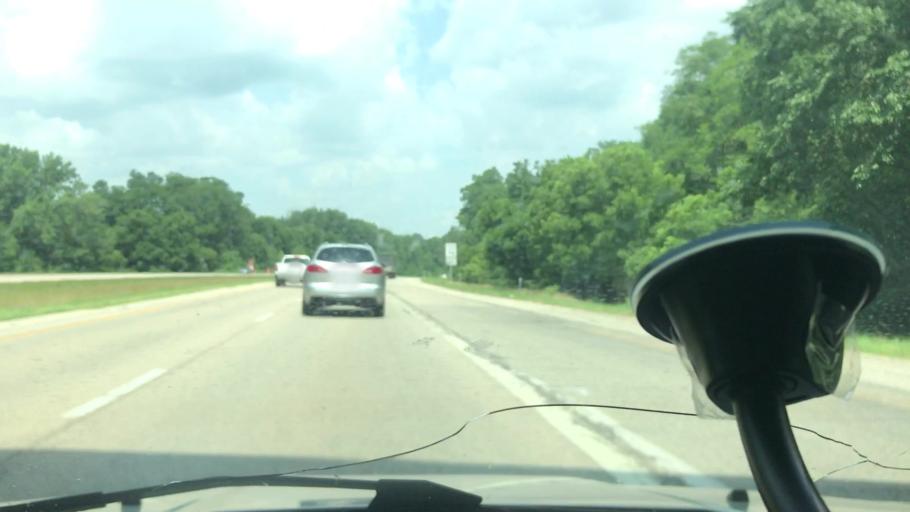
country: US
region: Illinois
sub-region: Peoria County
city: Bellevue
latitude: 40.6733
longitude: -89.6696
